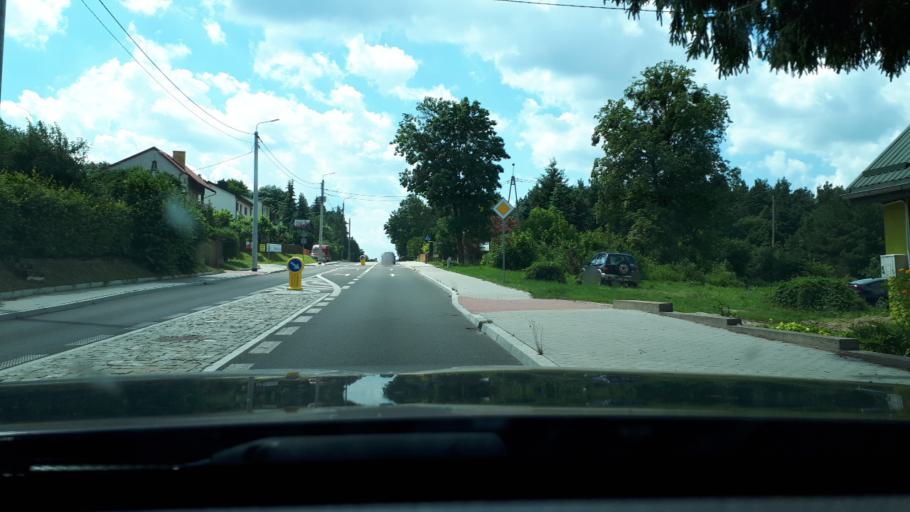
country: PL
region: Podlasie
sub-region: Powiat bialostocki
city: Suprasl
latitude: 53.2071
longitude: 23.3236
